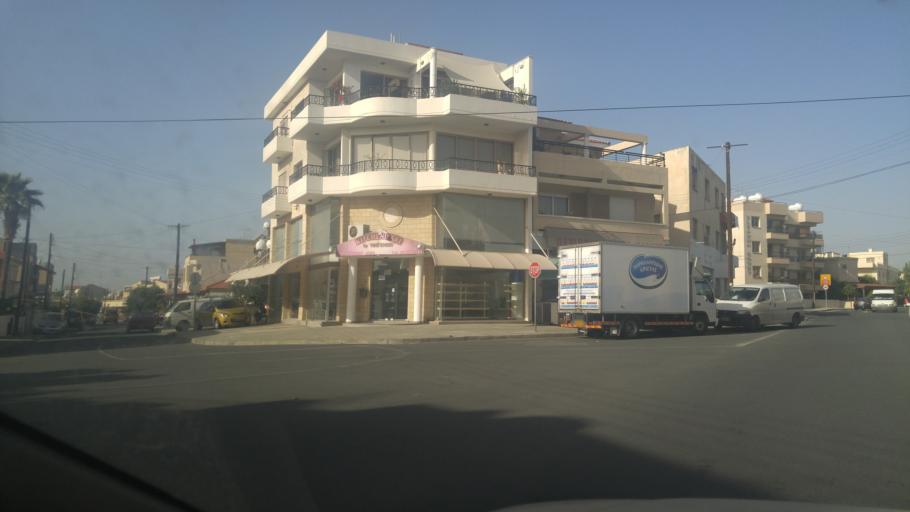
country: CY
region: Limassol
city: Limassol
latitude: 34.6827
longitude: 33.0199
